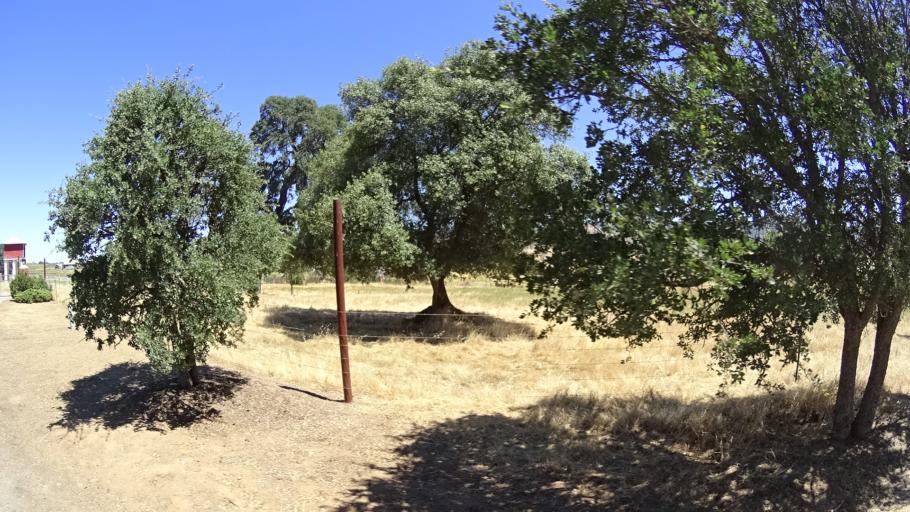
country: US
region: California
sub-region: Calaveras County
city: Copperopolis
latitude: 38.0349
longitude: -120.7218
